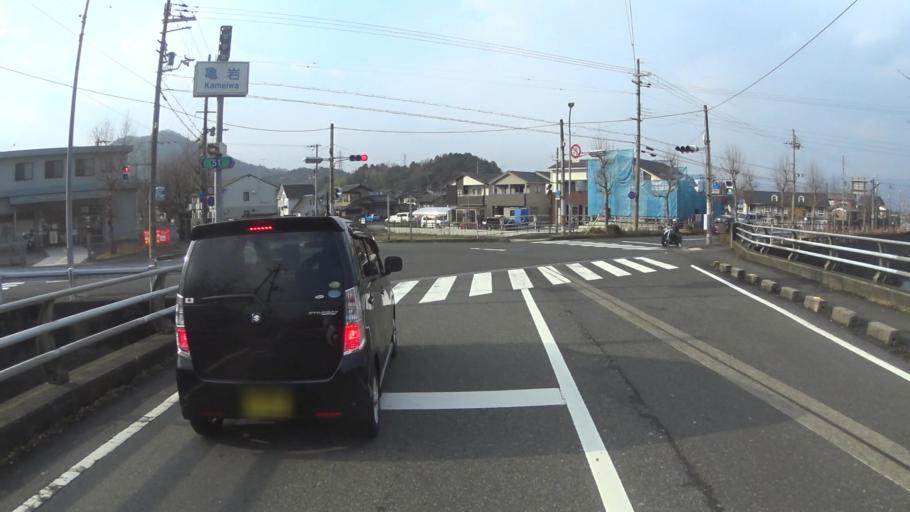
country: JP
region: Kyoto
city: Maizuru
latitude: 35.4495
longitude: 135.4116
